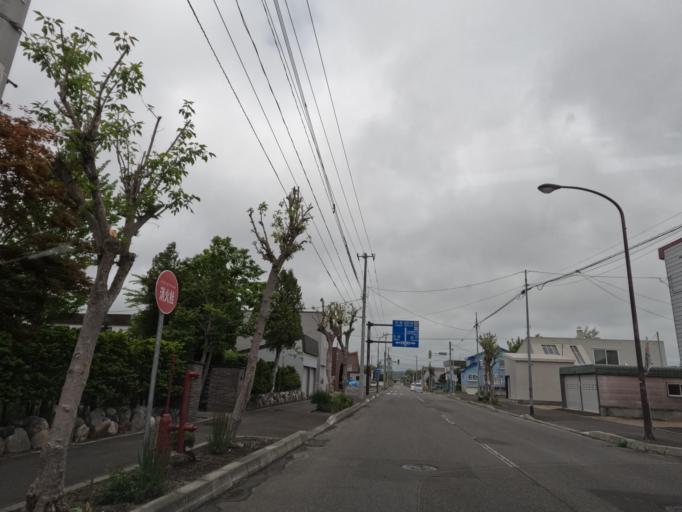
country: JP
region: Hokkaido
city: Tobetsu
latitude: 43.2248
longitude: 141.5178
